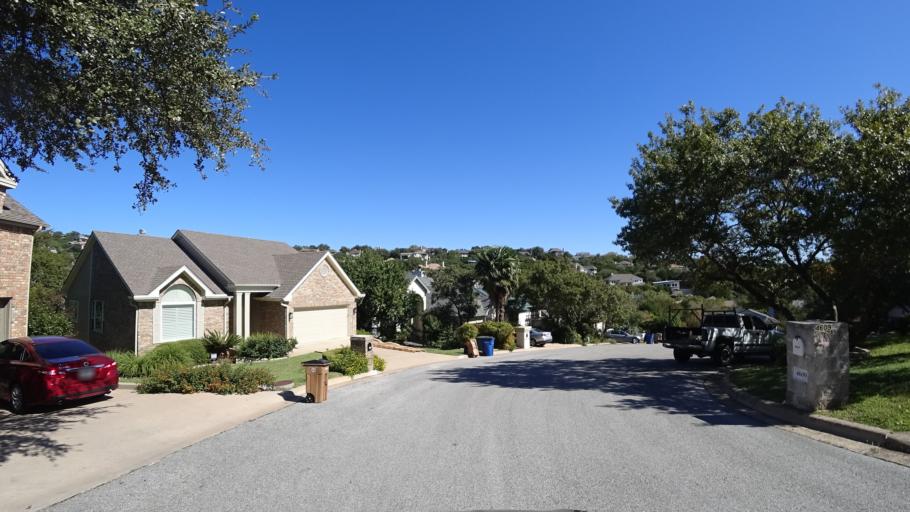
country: US
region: Texas
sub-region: Travis County
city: West Lake Hills
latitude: 30.3453
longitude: -97.7798
